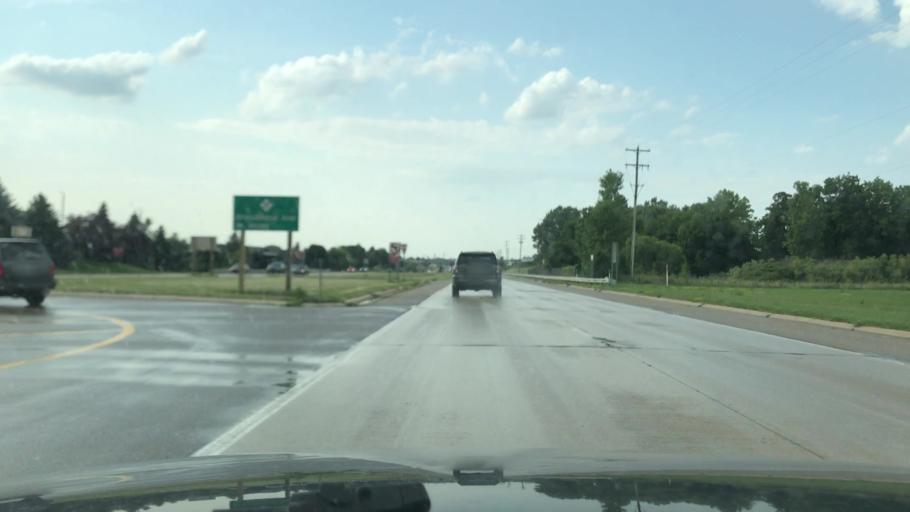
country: US
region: Michigan
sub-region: Kent County
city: East Grand Rapids
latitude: 42.8787
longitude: -85.5611
